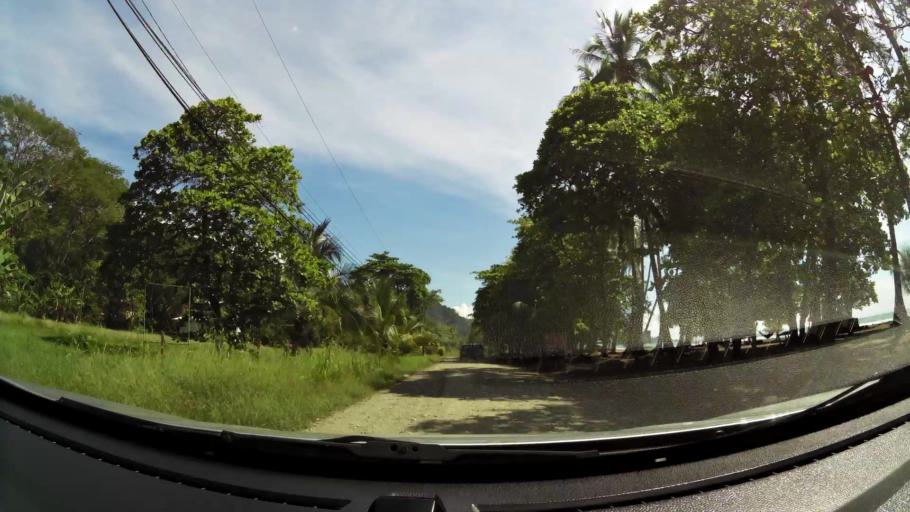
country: CR
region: San Jose
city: San Isidro
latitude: 9.2512
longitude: -83.8633
